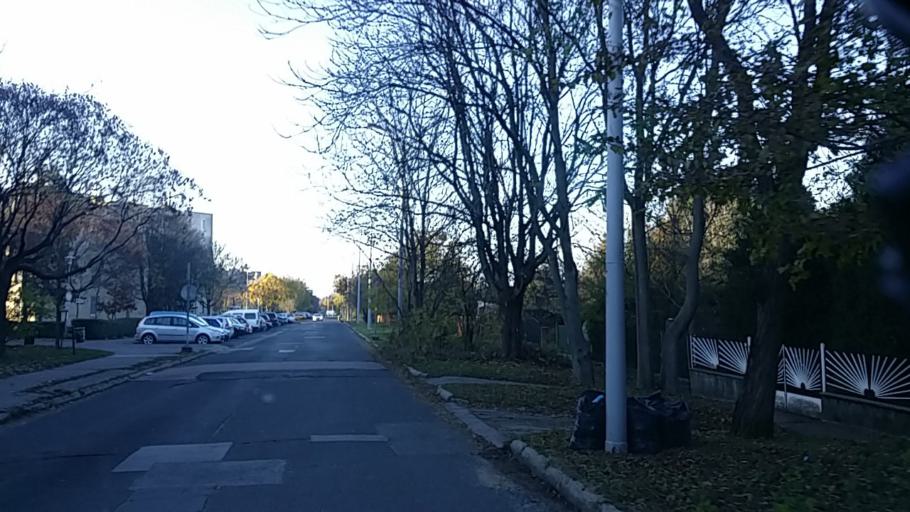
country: HU
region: Budapest
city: Budapest XVI. keruelet
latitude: 47.5167
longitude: 19.1883
